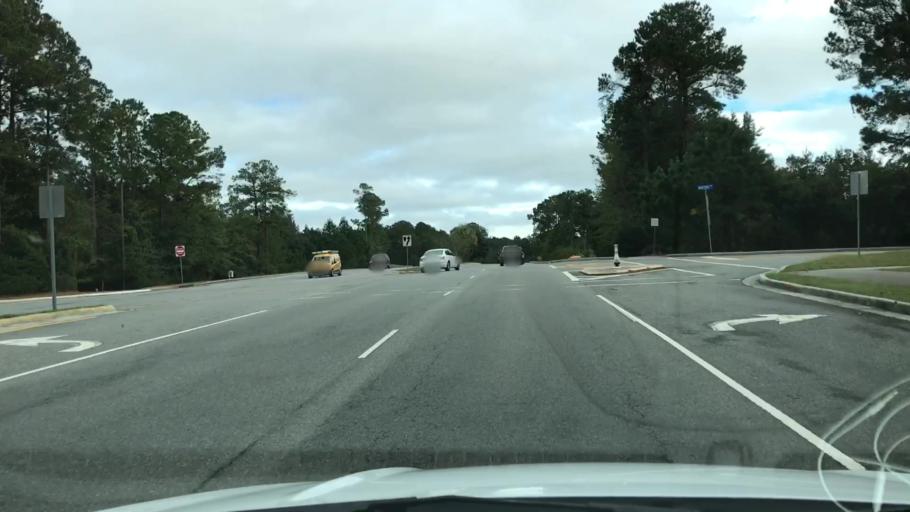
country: US
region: South Carolina
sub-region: Beaufort County
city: Bluffton
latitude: 32.2578
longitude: -80.8960
